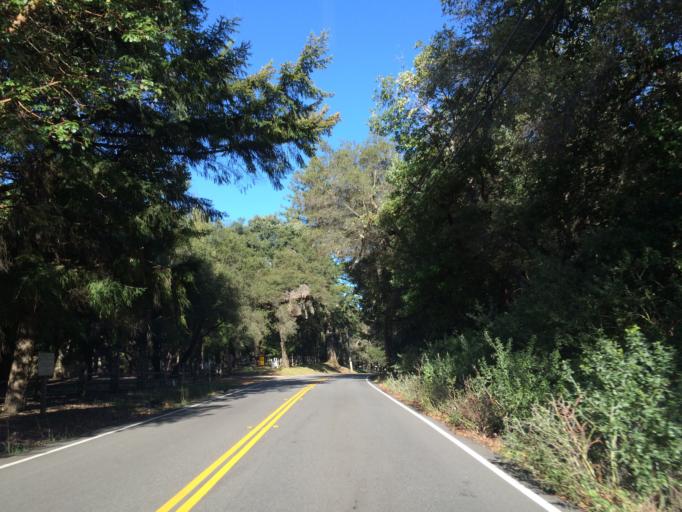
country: US
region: California
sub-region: Santa Cruz County
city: Boulder Creek
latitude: 37.1290
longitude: -122.1658
